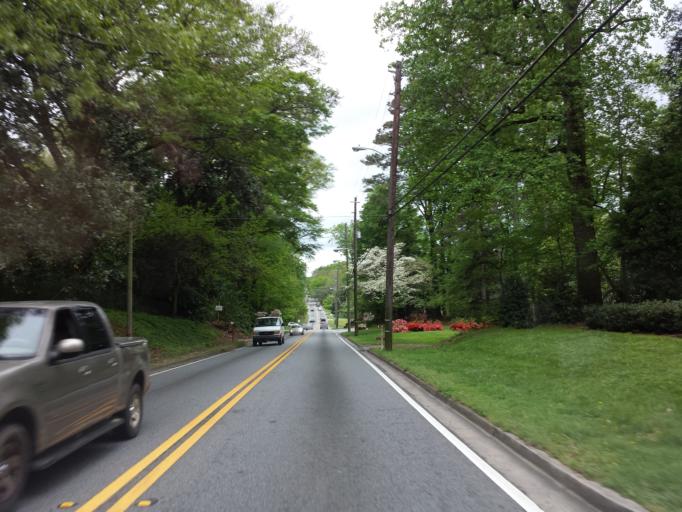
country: US
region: Georgia
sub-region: Cobb County
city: Marietta
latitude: 33.9518
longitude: -84.5619
